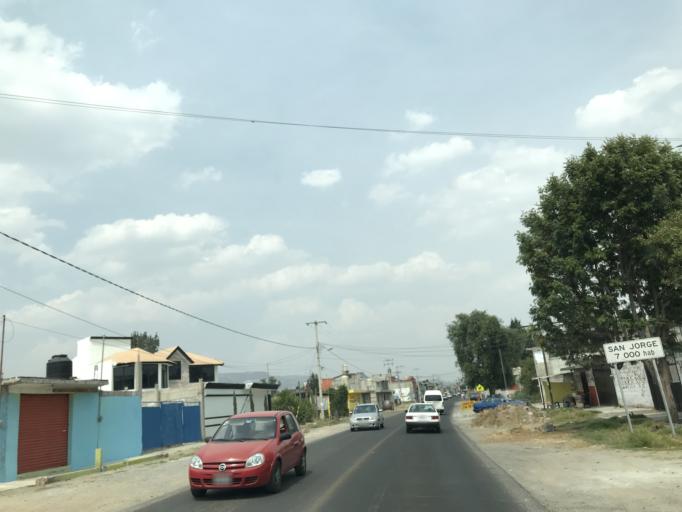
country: MX
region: Tlaxcala
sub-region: Ixtacuixtla de Mariano Matamoros
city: Santa Justina Ecatepec
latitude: 19.3177
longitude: -98.3182
